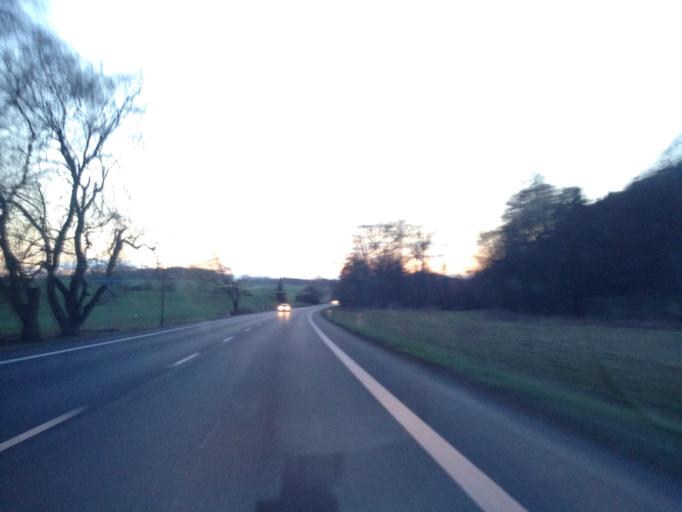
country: CZ
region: Central Bohemia
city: Jesenice
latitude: 50.1377
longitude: 13.4592
